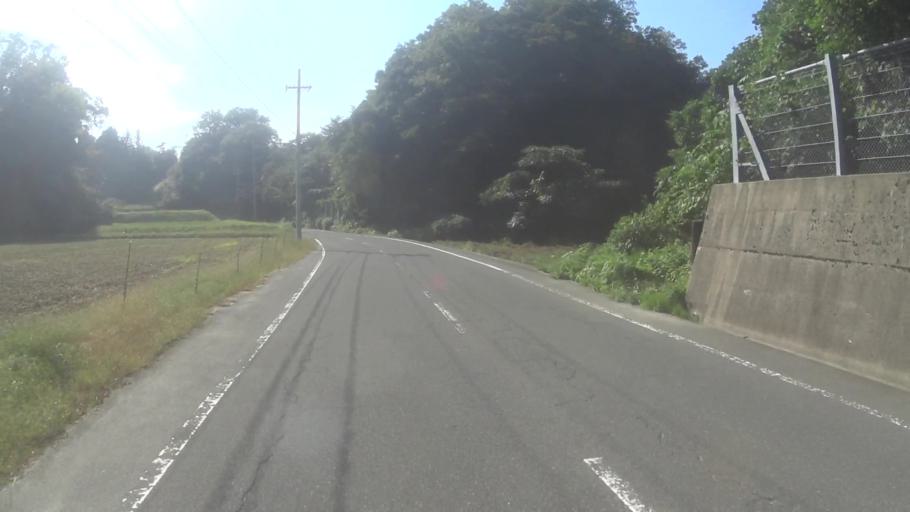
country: JP
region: Kyoto
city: Miyazu
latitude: 35.6906
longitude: 135.1254
